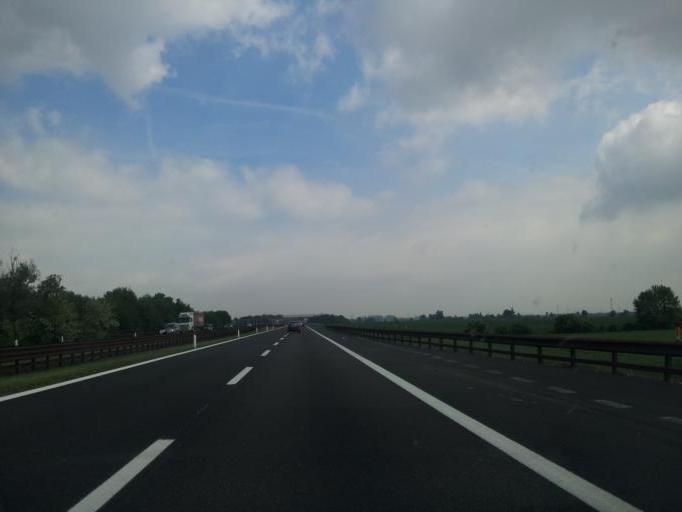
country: IT
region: Veneto
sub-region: Provincia di Verona
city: Nogarole Rocca
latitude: 45.3083
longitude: 10.9064
